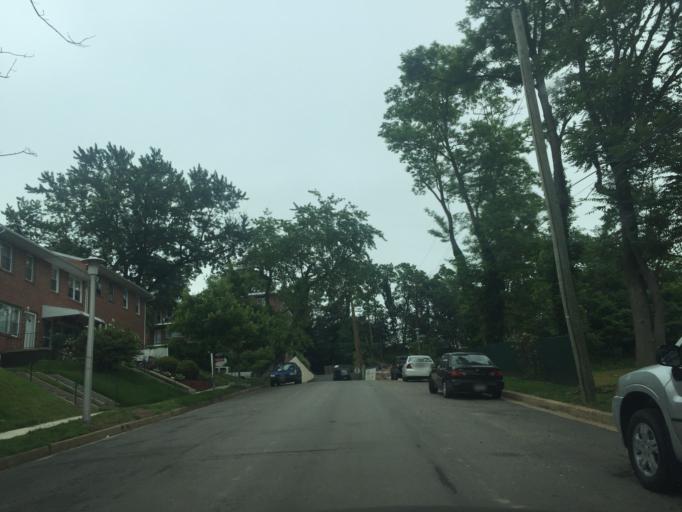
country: US
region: Maryland
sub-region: City of Baltimore
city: Baltimore
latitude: 39.3396
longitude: -76.6381
